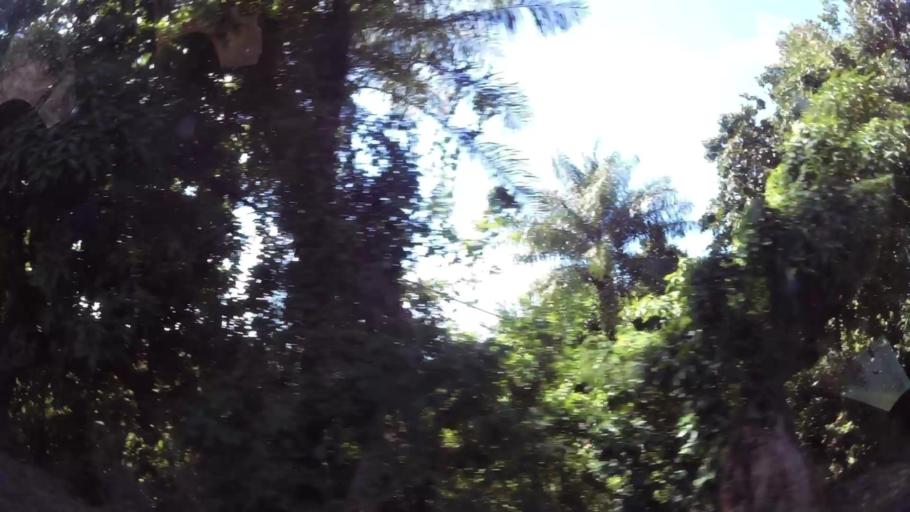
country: DM
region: Saint Paul
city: Mahaut
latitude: 15.3395
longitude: -61.3858
